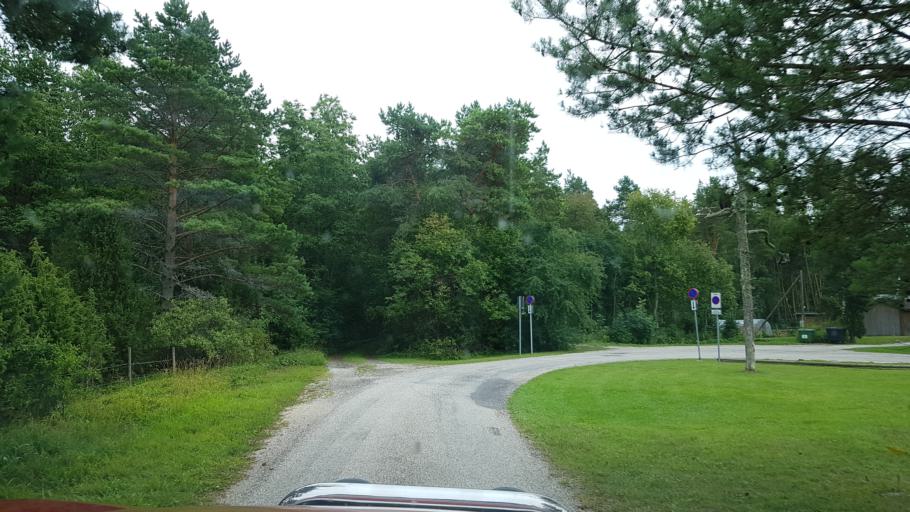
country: EE
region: Laeaene
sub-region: Ridala Parish
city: Uuemoisa
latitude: 58.9988
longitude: 23.6381
